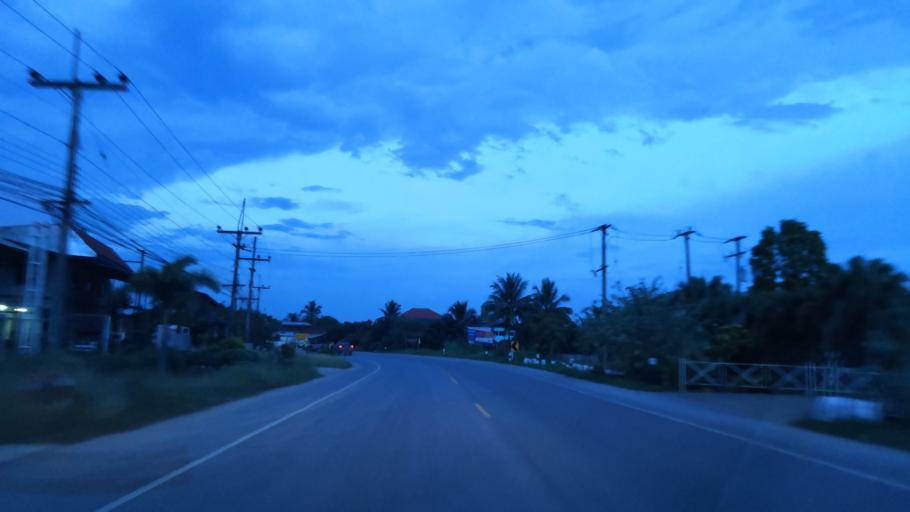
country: TH
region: Chiang Rai
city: Wiang Chiang Rung
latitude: 19.9727
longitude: 100.0156
